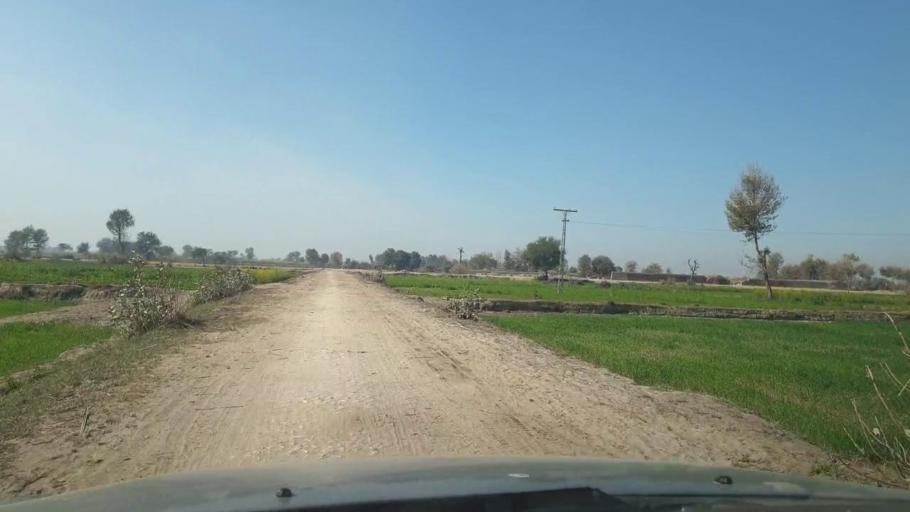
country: PK
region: Sindh
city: Ghotki
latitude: 28.0335
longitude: 69.2479
